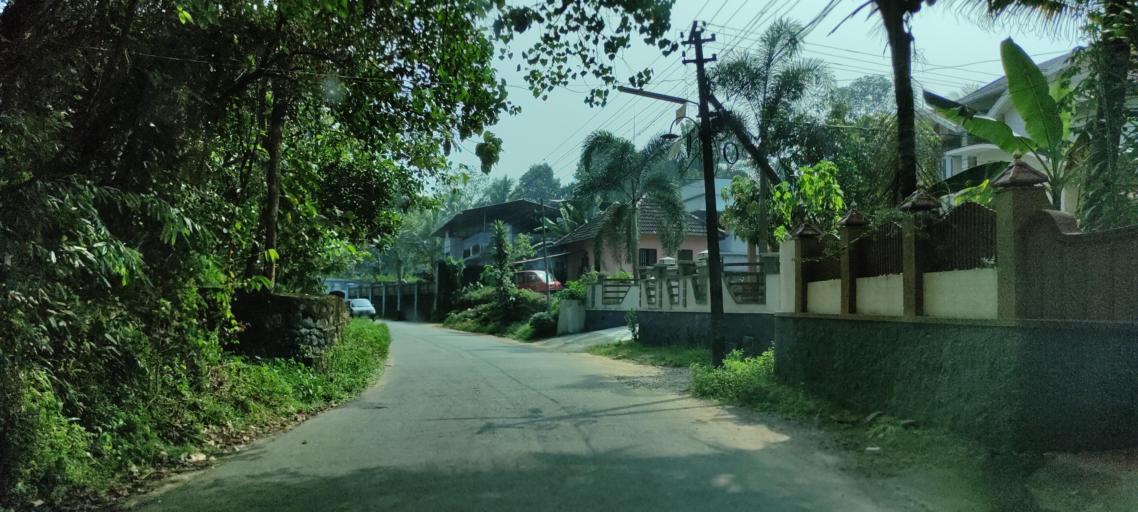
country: IN
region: Kerala
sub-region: Pattanamtitta
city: Adur
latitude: 9.2238
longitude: 76.7133
